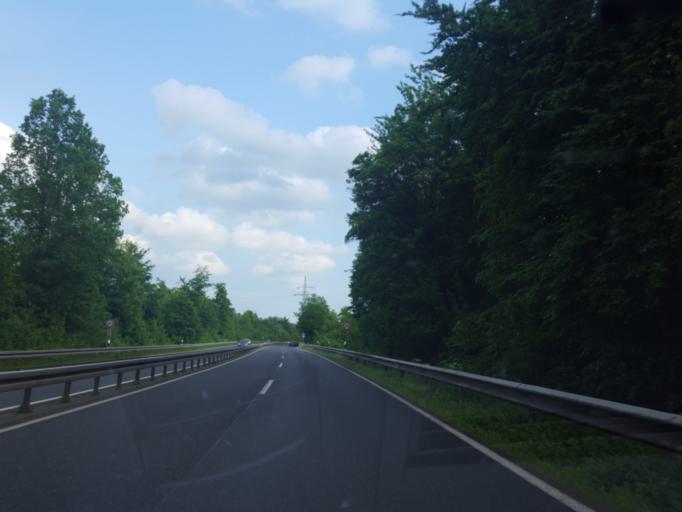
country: DE
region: Lower Saxony
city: Gittelde
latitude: 51.8021
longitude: 10.1912
